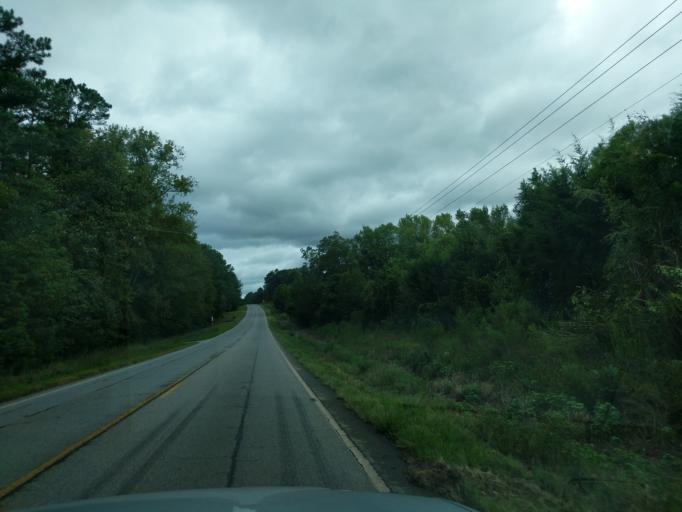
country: US
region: Georgia
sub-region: Wilkes County
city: Washington
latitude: 33.6886
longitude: -82.6611
